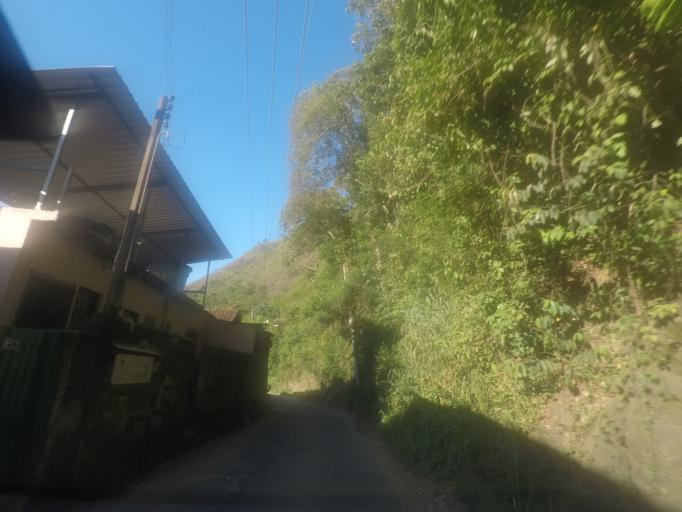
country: BR
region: Rio de Janeiro
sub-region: Petropolis
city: Petropolis
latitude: -22.4958
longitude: -43.1492
